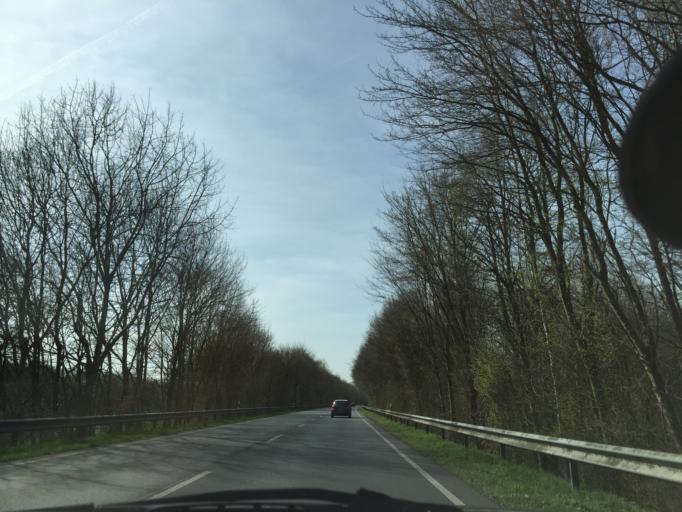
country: DE
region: North Rhine-Westphalia
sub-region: Regierungsbezirk Dusseldorf
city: Goch
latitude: 51.6957
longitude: 6.1333
